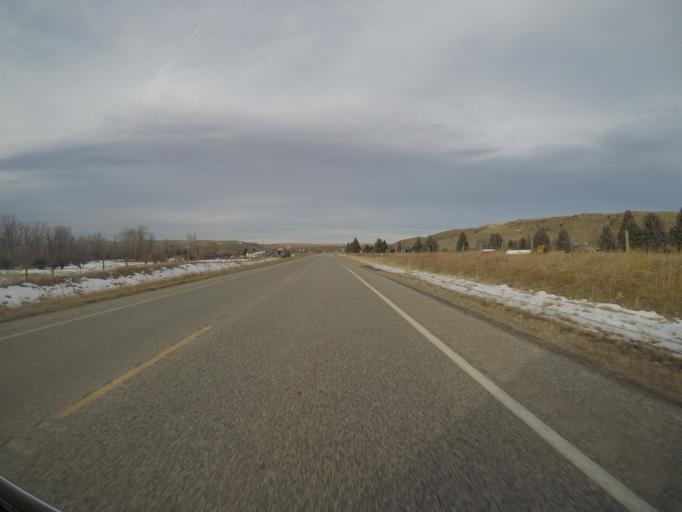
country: US
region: Montana
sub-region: Stillwater County
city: Absarokee
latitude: 45.4781
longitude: -109.4496
